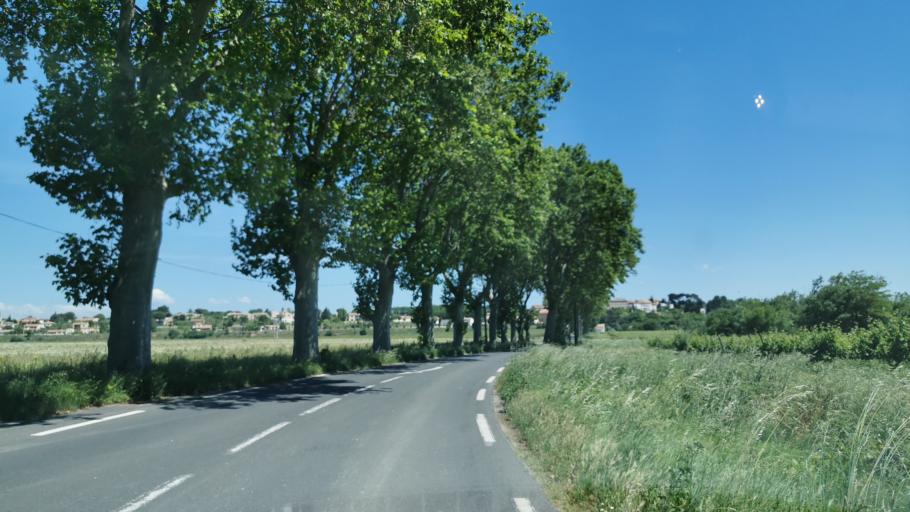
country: FR
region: Languedoc-Roussillon
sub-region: Departement de l'Aude
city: Canet
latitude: 43.2423
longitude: 2.8548
